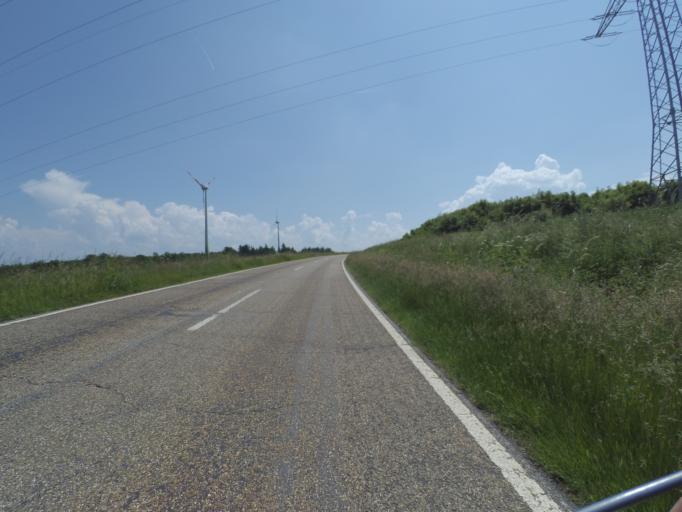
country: DE
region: Rheinland-Pfalz
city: Hambuch
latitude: 50.2379
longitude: 7.1800
